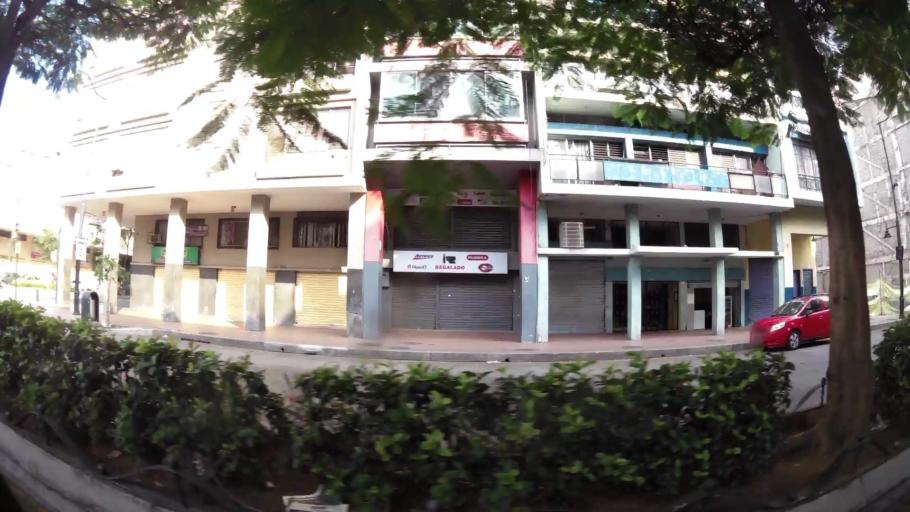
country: EC
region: Guayas
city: Guayaquil
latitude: -2.1965
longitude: -79.8832
